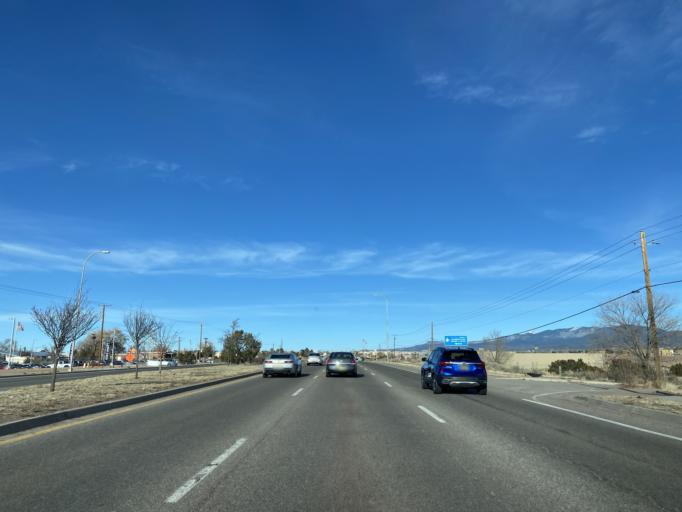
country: US
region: New Mexico
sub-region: Santa Fe County
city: Agua Fria
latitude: 35.6226
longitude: -106.0273
